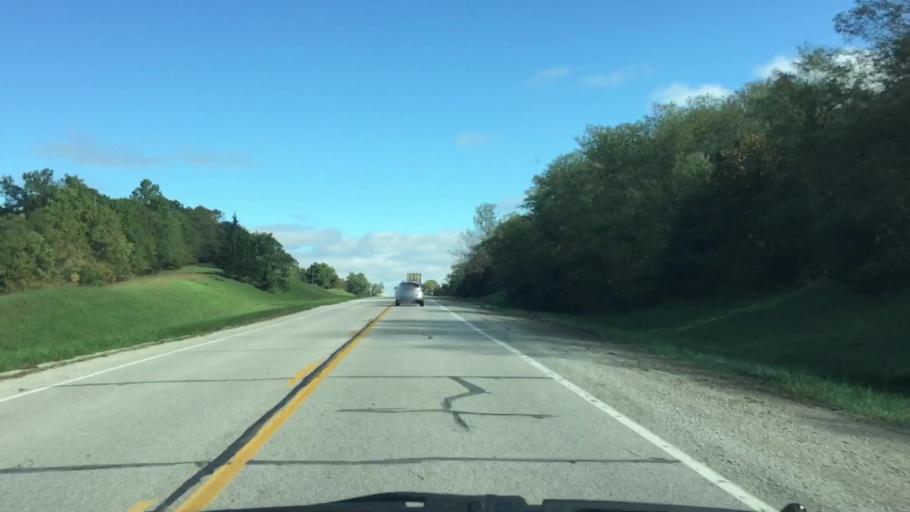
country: US
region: Iowa
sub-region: Decatur County
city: Leon
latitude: 40.6561
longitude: -93.7979
